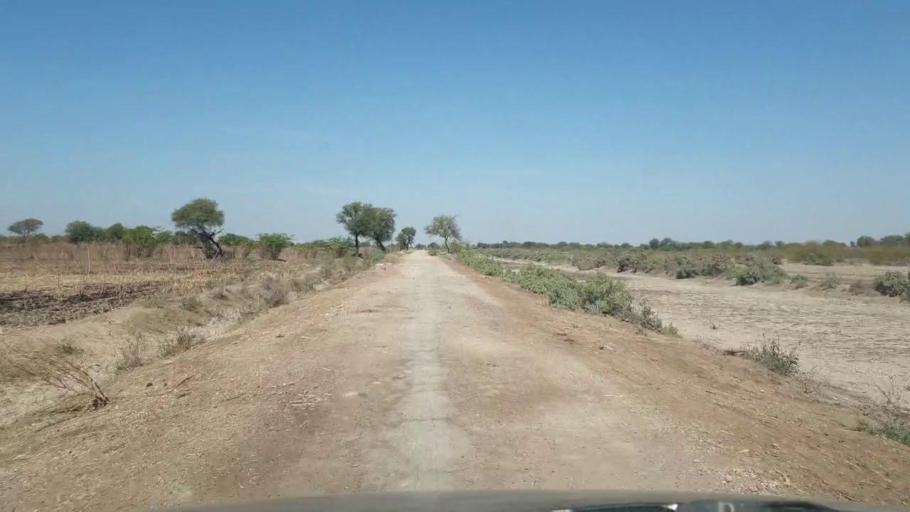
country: PK
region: Sindh
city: Dhoro Naro
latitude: 25.4270
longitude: 69.6204
